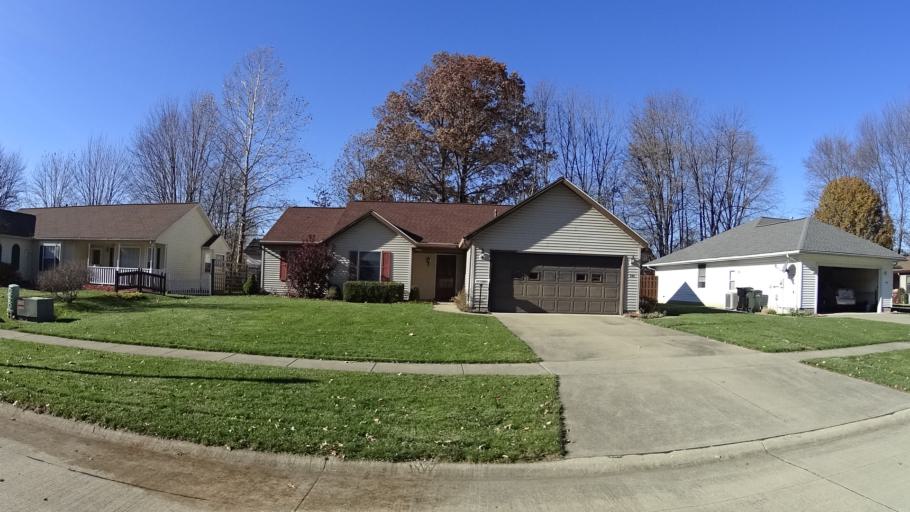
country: US
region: Ohio
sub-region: Lorain County
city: Elyria
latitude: 41.3467
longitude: -82.0770
